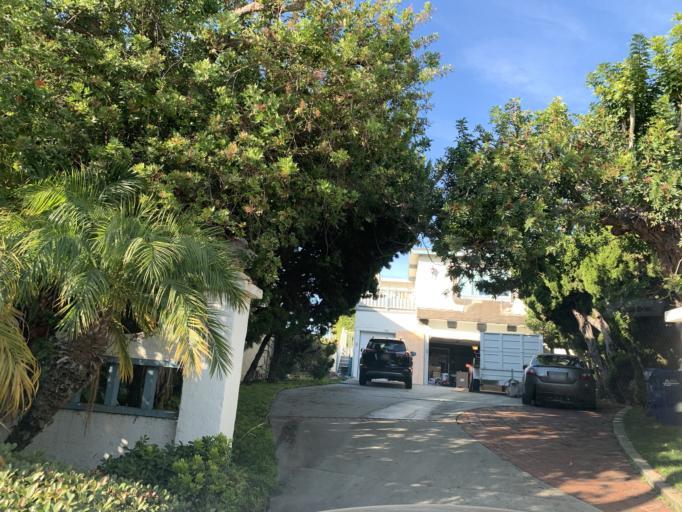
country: US
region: California
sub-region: Los Angeles County
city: Hermosa Beach
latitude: 33.8676
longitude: -118.3920
